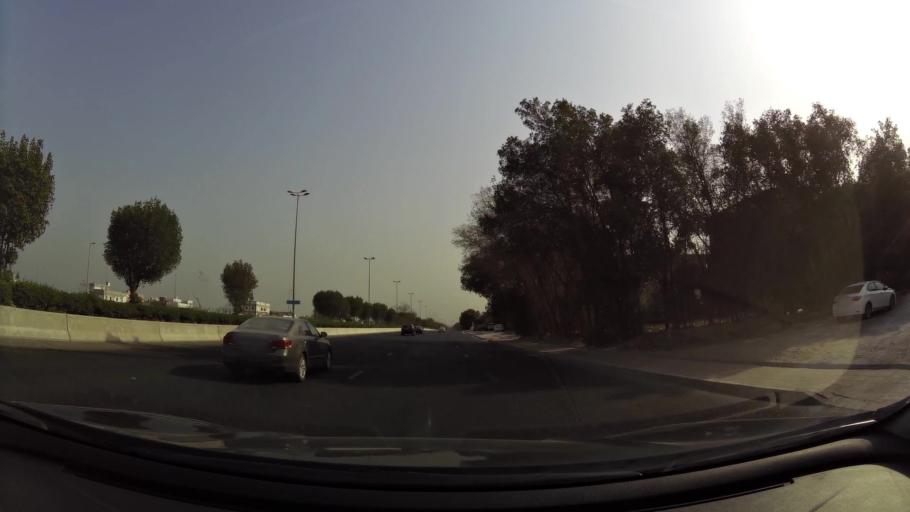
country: KW
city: Al Funaytis
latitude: 29.2193
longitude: 48.0874
